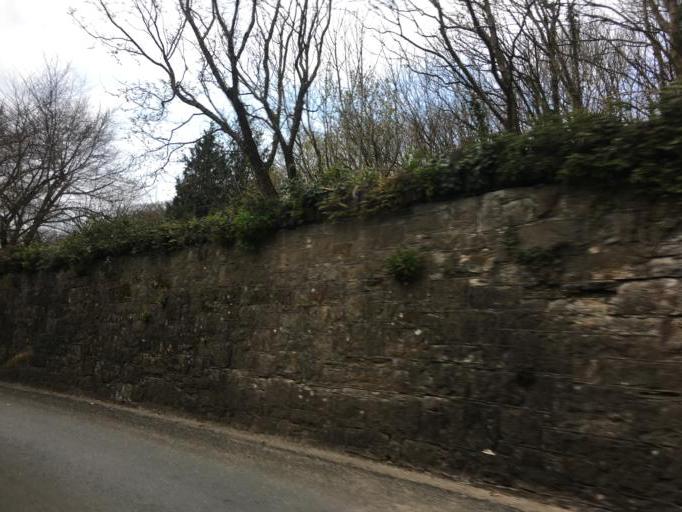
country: GB
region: Wales
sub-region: Gwynedd
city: Y Felinheli
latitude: 53.1917
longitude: -4.1941
